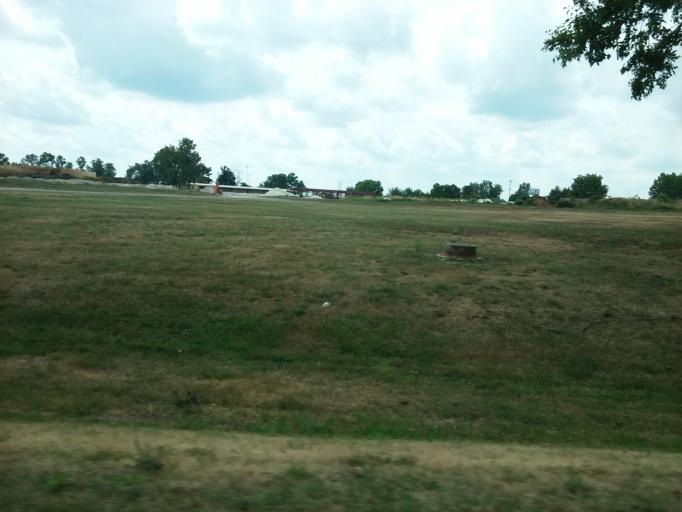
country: US
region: Ohio
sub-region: Hancock County
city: Findlay
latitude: 41.0507
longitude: -83.6701
